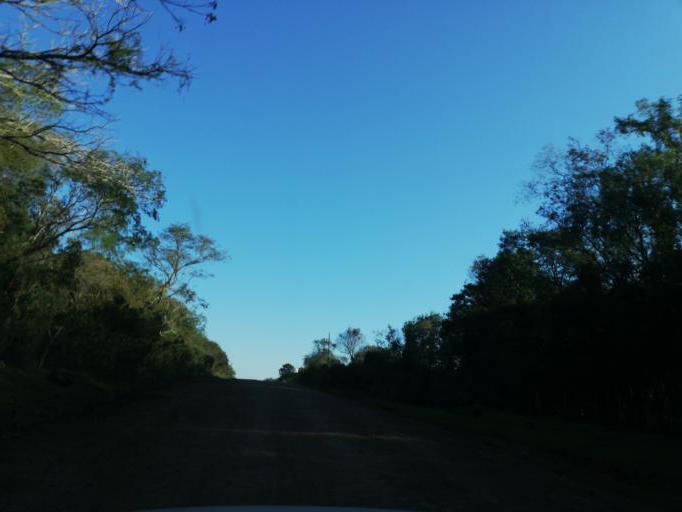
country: AR
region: Misiones
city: Cerro Cora
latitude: -27.5831
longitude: -55.6873
